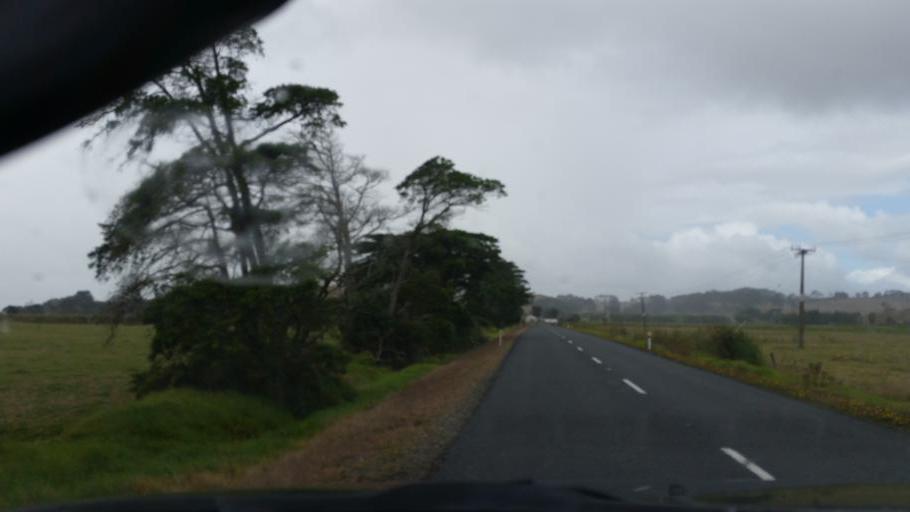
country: NZ
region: Northland
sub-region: Kaipara District
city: Dargaville
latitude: -36.1107
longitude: 173.9563
